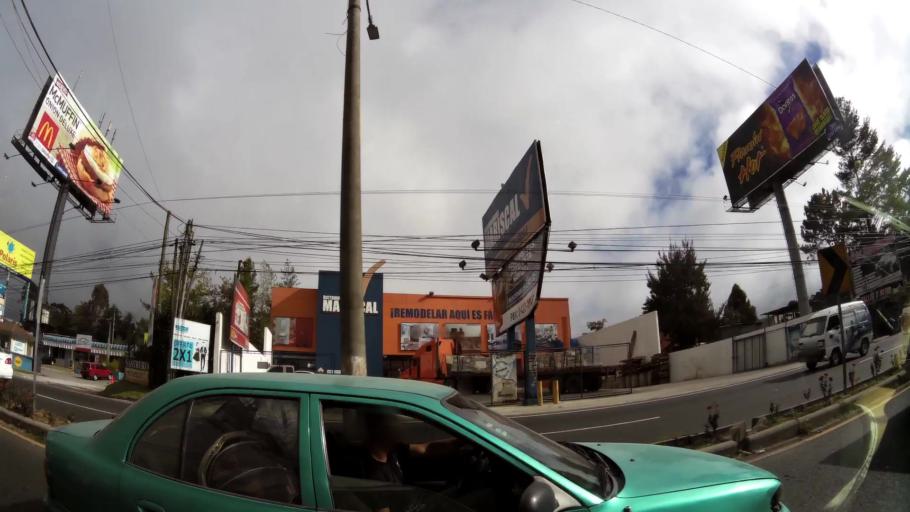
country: GT
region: Guatemala
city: Santa Catarina Pinula
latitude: 14.5638
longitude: -90.4644
